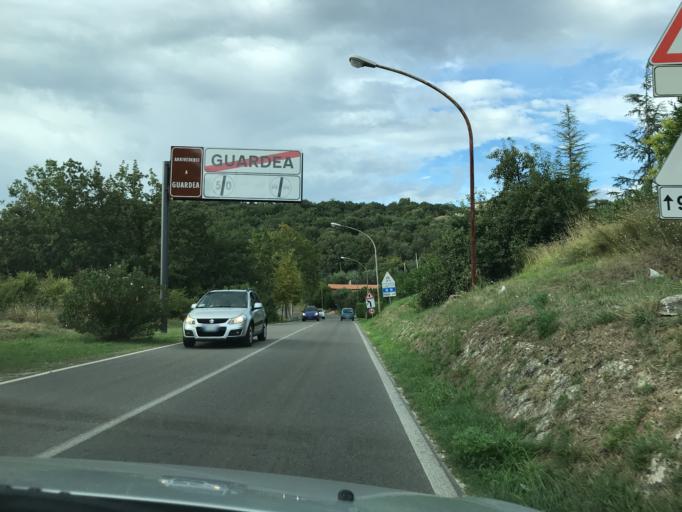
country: IT
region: Umbria
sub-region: Provincia di Terni
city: Guardea
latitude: 42.6289
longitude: 12.2964
